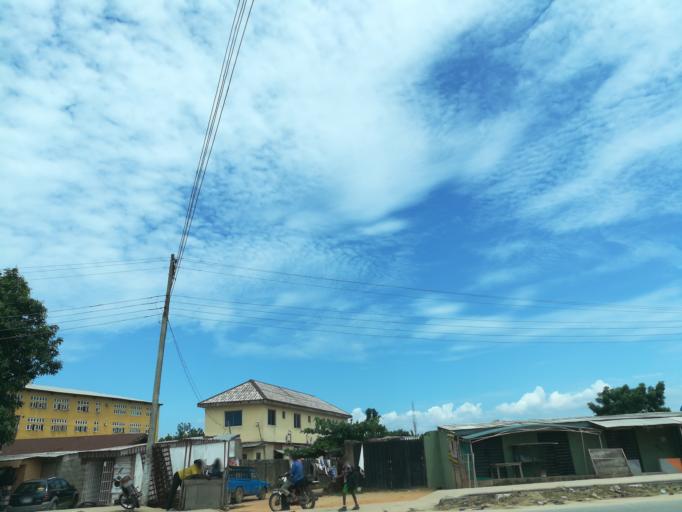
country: NG
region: Lagos
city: Ebute Ikorodu
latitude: 6.5630
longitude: 3.4770
